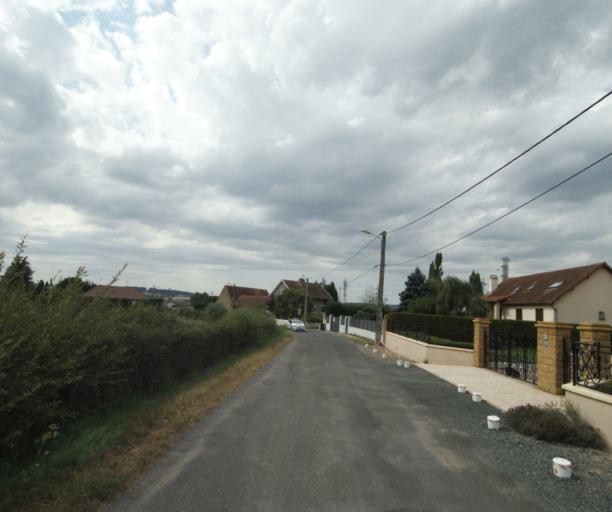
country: FR
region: Bourgogne
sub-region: Departement de Saone-et-Loire
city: Gueugnon
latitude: 46.6074
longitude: 4.0779
